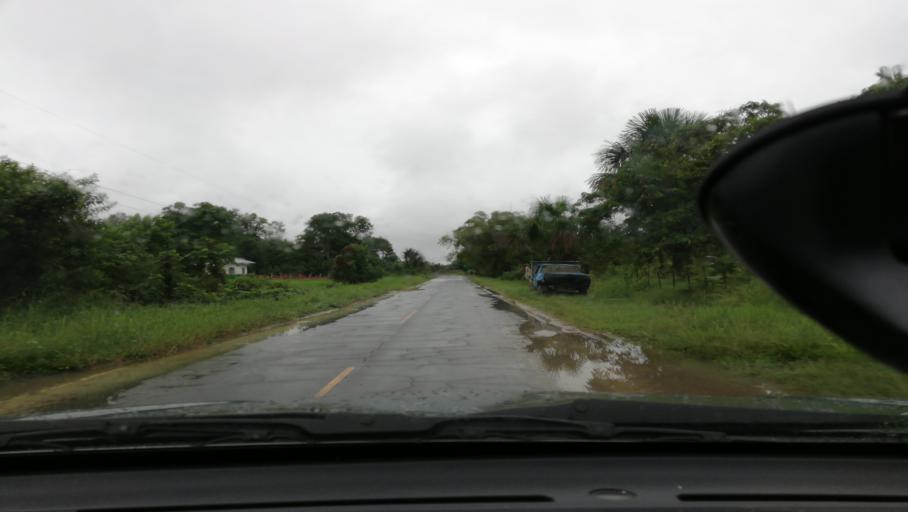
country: PE
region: Loreto
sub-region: Provincia de Maynas
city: San Juan
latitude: -4.1585
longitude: -73.4735
